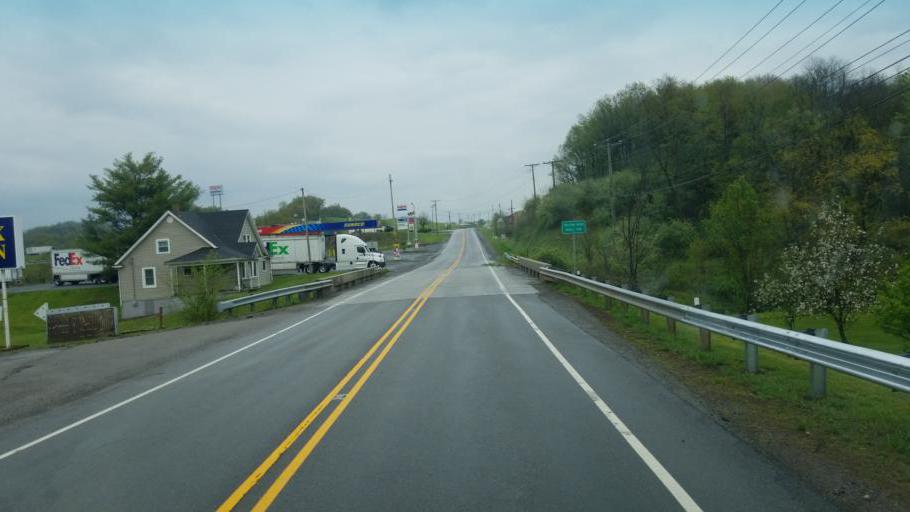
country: US
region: Virginia
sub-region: Smyth County
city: Atkins
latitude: 36.8853
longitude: -81.3739
